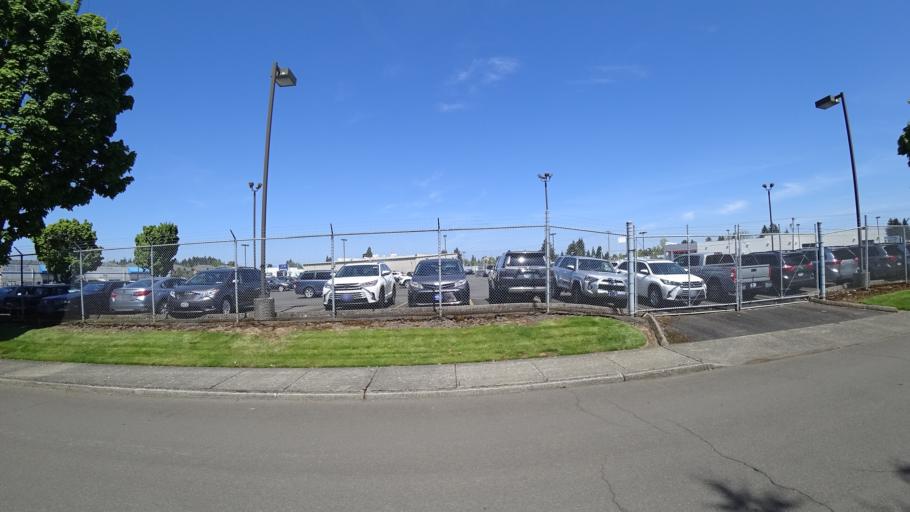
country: US
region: Oregon
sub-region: Washington County
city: Hillsboro
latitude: 45.5076
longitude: -122.9687
